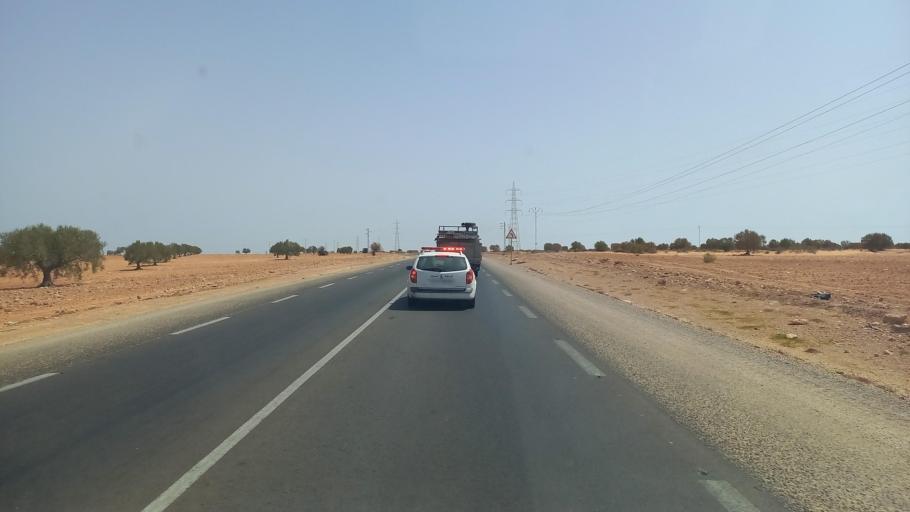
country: TN
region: Madanin
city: Zarzis
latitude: 33.4040
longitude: 10.8542
